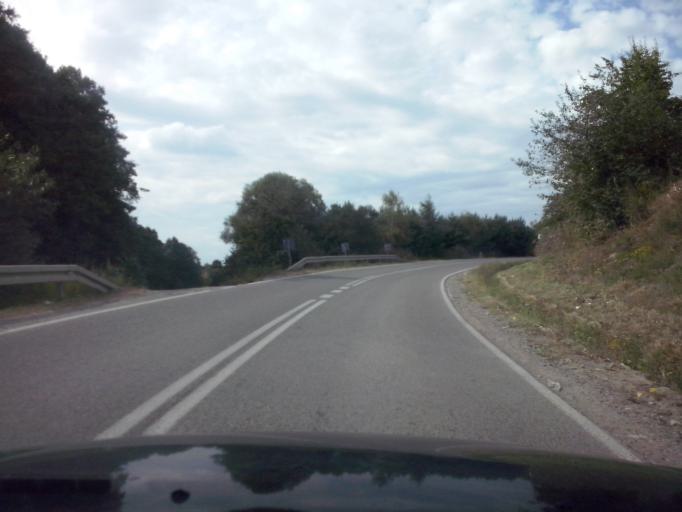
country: PL
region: Swietokrzyskie
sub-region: Powiat kielecki
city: Lagow
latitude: 50.7821
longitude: 21.0831
